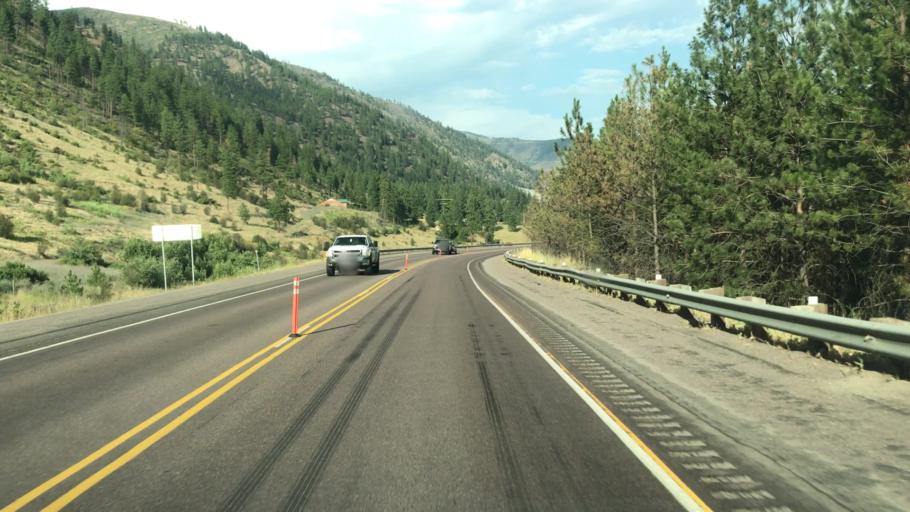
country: US
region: Montana
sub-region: Mineral County
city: Superior
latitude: 47.0182
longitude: -114.6809
